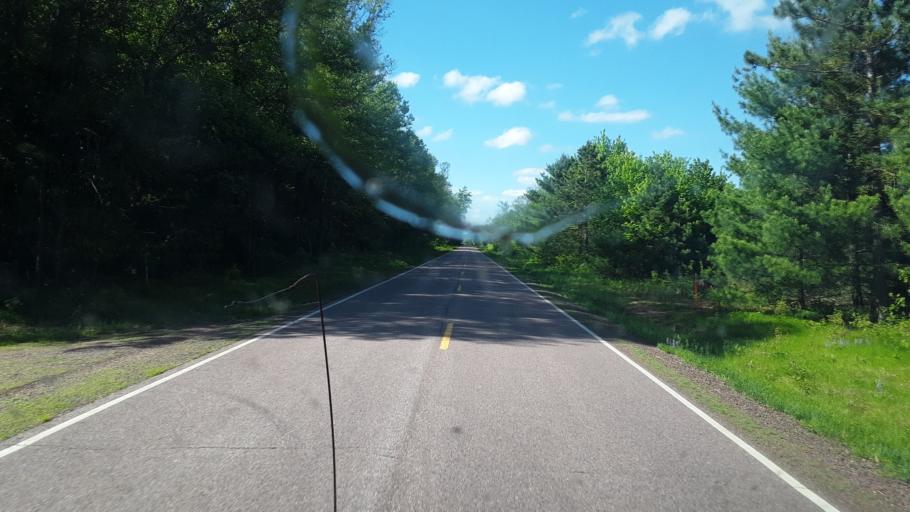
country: US
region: Wisconsin
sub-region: Wood County
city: Nekoosa
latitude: 44.3655
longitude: -90.1301
